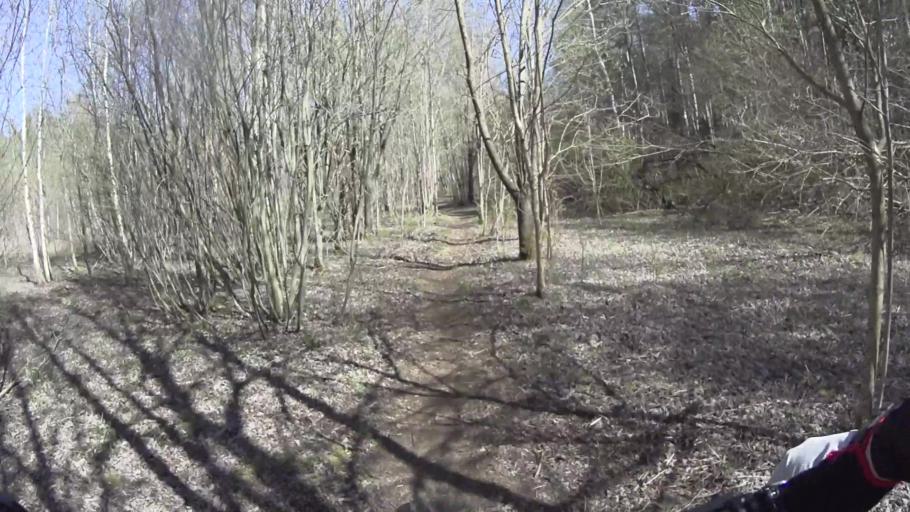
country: LV
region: Riga
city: Daugavgriva
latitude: 56.9778
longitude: 23.9877
